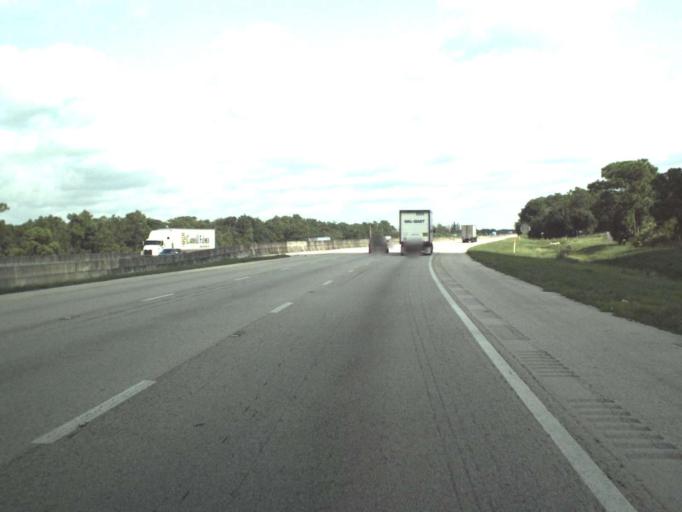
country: US
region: Florida
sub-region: Palm Beach County
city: Limestone Creek
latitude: 26.9514
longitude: -80.1625
